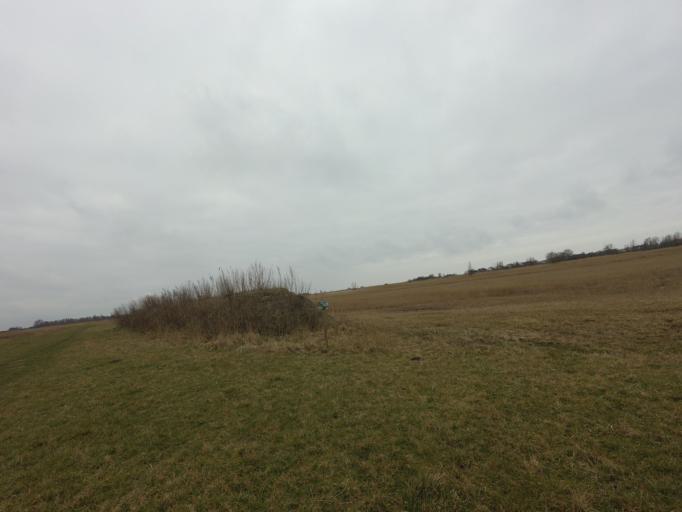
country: NL
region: Friesland
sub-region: Sudwest Fryslan
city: Makkum
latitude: 53.0477
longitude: 5.3972
